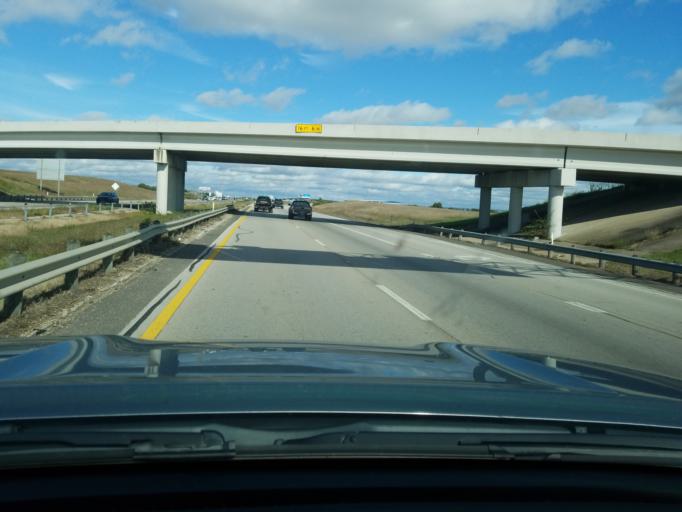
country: US
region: Texas
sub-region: Tarrant County
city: White Settlement
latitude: 32.7330
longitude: -97.4956
